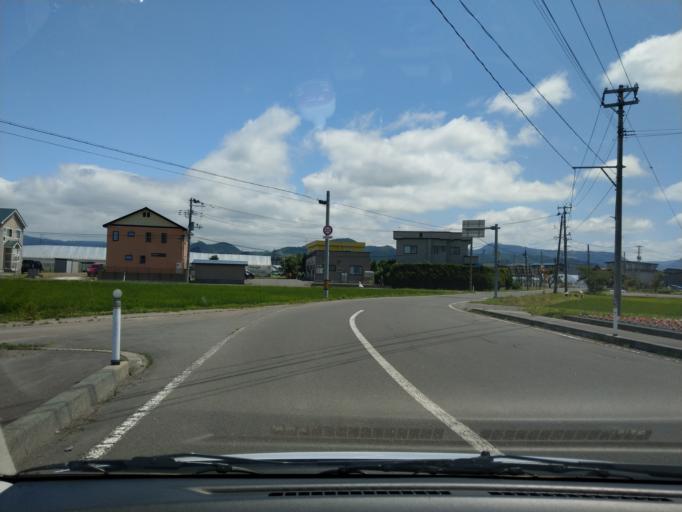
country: JP
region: Aomori
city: Kuroishi
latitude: 40.5768
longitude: 140.5516
